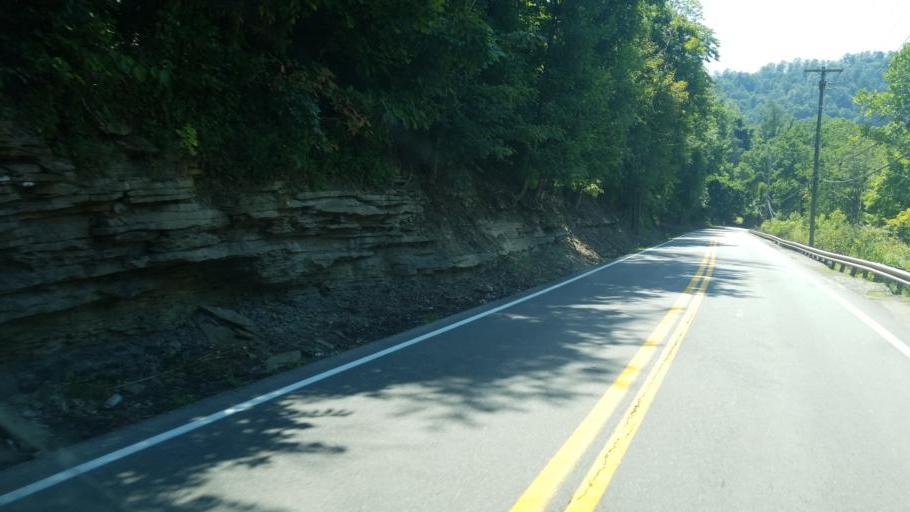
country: US
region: West Virginia
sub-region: Kanawha County
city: Chesapeake
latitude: 38.1835
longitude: -81.4712
